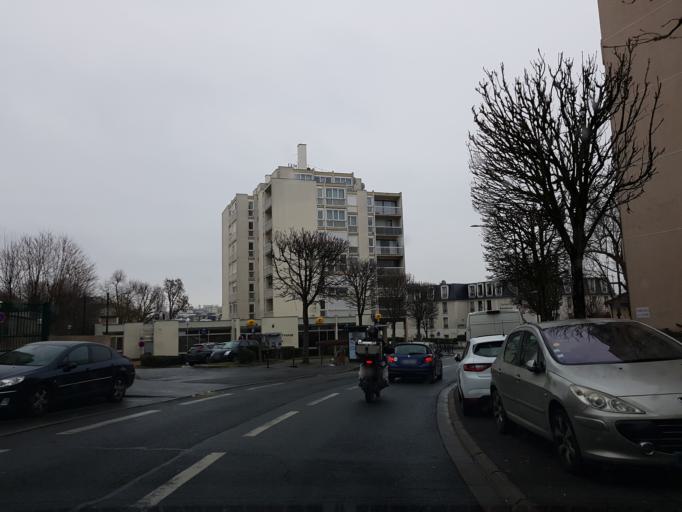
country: FR
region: Ile-de-France
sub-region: Departement du Val-de-Marne
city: Thiais
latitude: 48.7644
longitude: 2.3930
